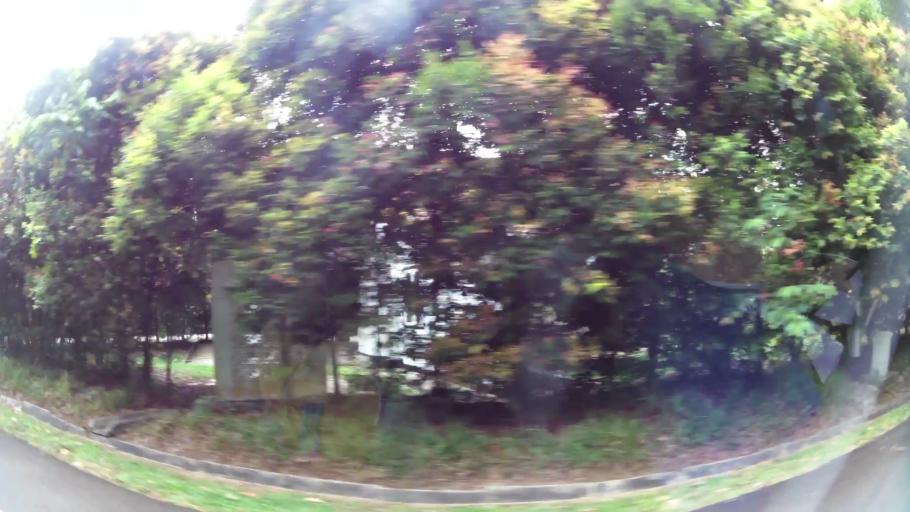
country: MY
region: Johor
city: Kampung Pasir Gudang Baru
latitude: 1.4579
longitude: 103.8336
